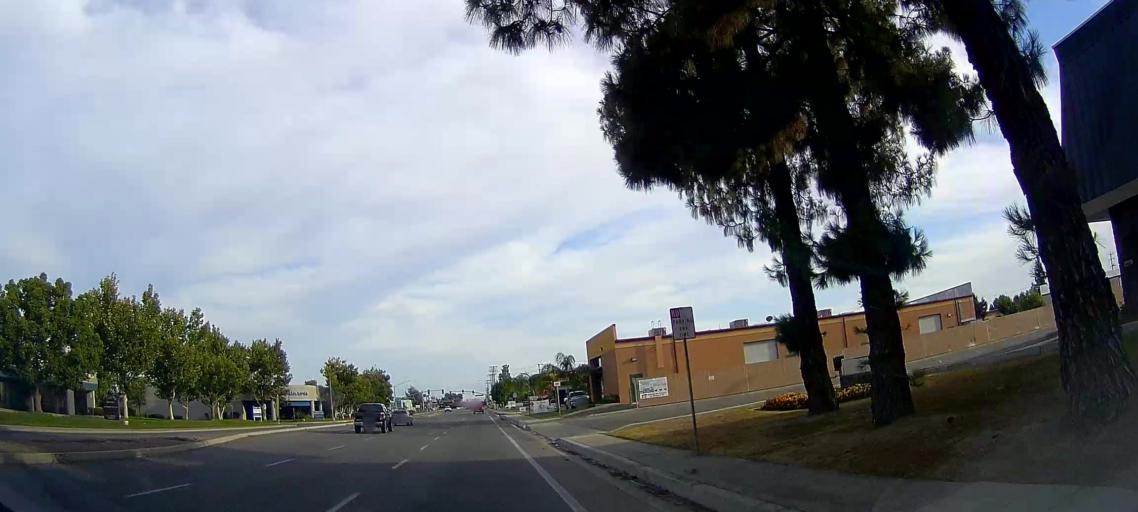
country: US
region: California
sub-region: Kern County
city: Bakersfield
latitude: 35.3150
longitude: -119.0568
